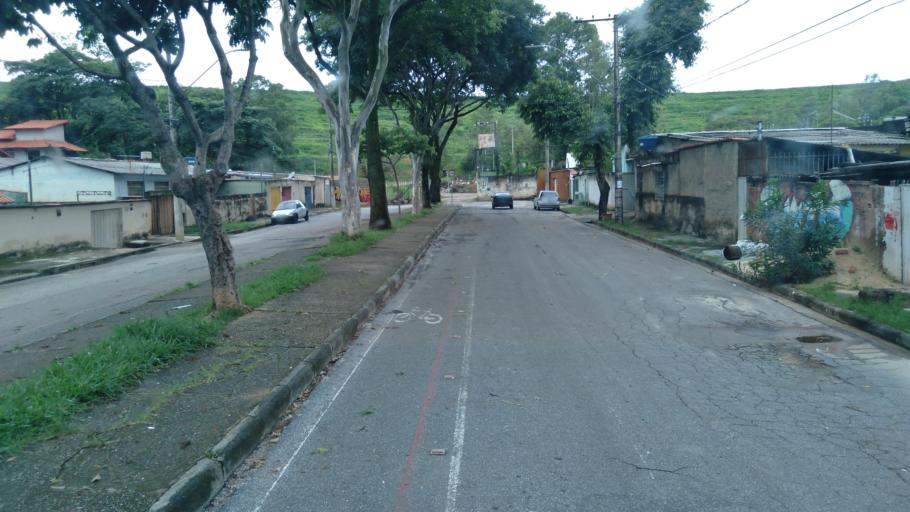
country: BR
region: Minas Gerais
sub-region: Contagem
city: Contagem
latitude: -19.9095
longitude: -44.0156
